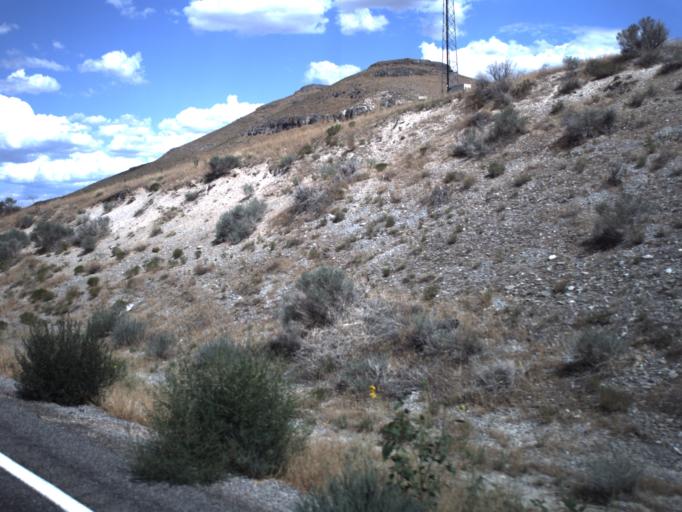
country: US
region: Utah
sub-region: Millard County
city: Delta
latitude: 39.6479
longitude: -112.2986
